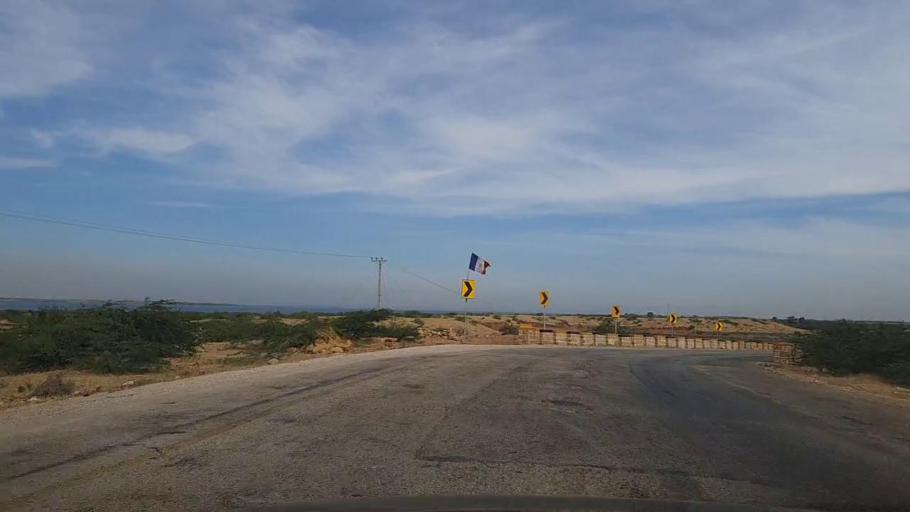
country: PK
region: Sindh
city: Thatta
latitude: 24.8697
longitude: 68.0336
